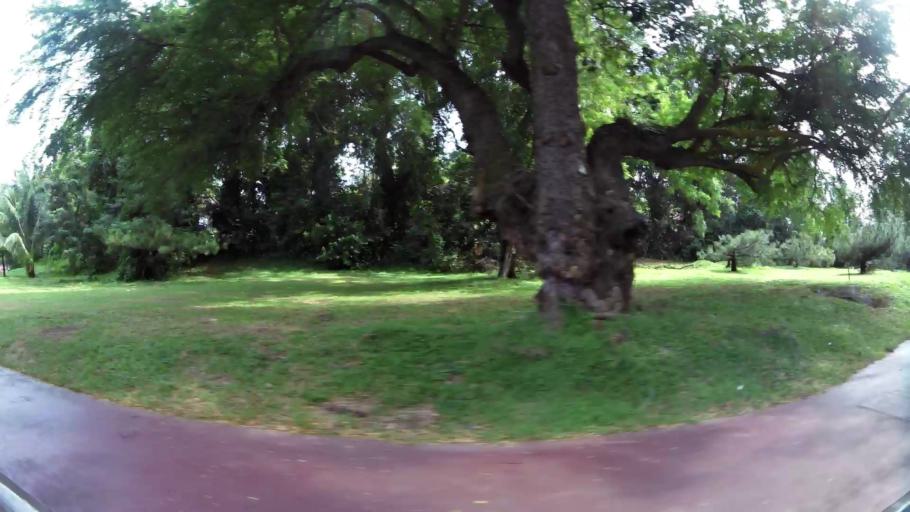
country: SG
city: Singapore
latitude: 1.3006
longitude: 103.7883
